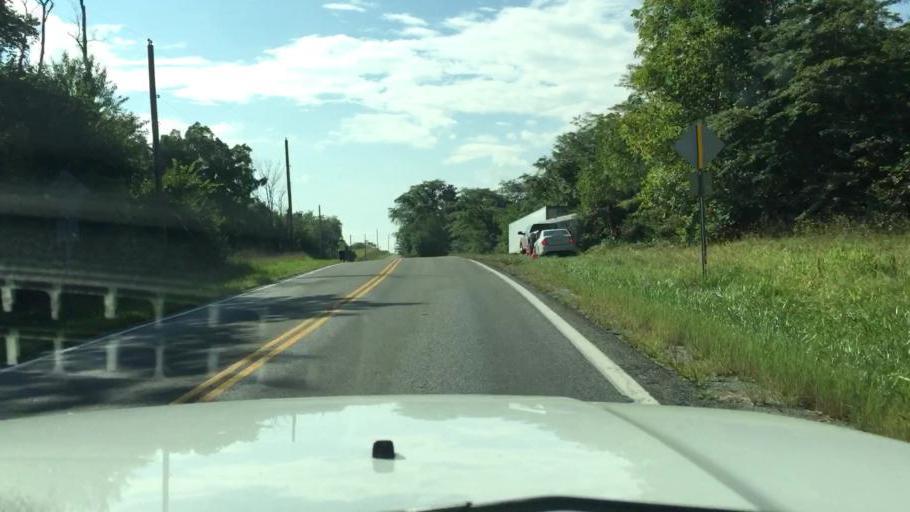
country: US
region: Ohio
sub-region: Champaign County
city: Mechanicsburg
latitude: 40.0391
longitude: -83.6046
